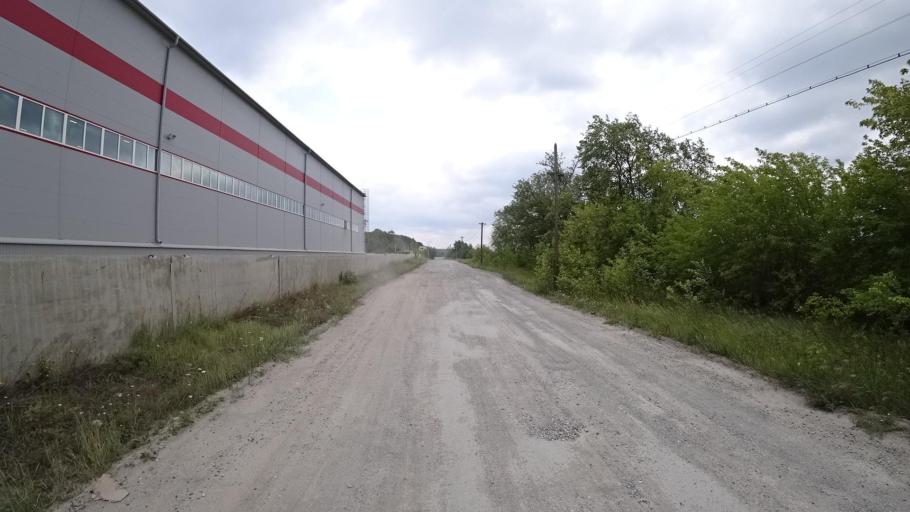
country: RU
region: Sverdlovsk
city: Kamyshlov
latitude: 56.8311
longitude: 62.7256
